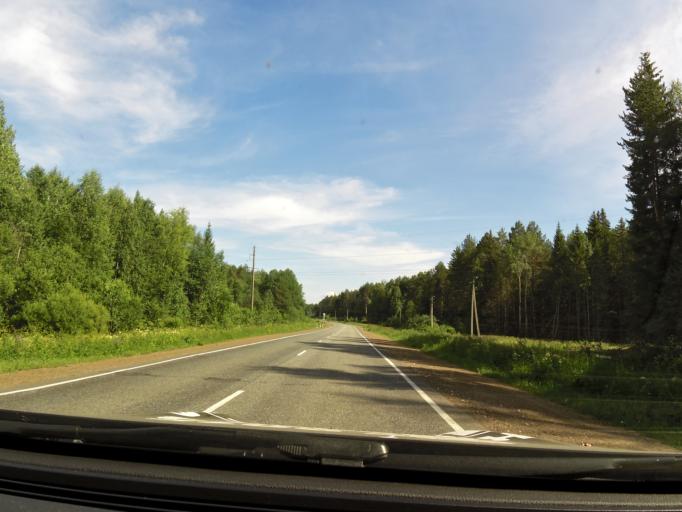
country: RU
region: Kirov
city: Belaya Kholunitsa
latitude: 58.8457
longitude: 50.7637
